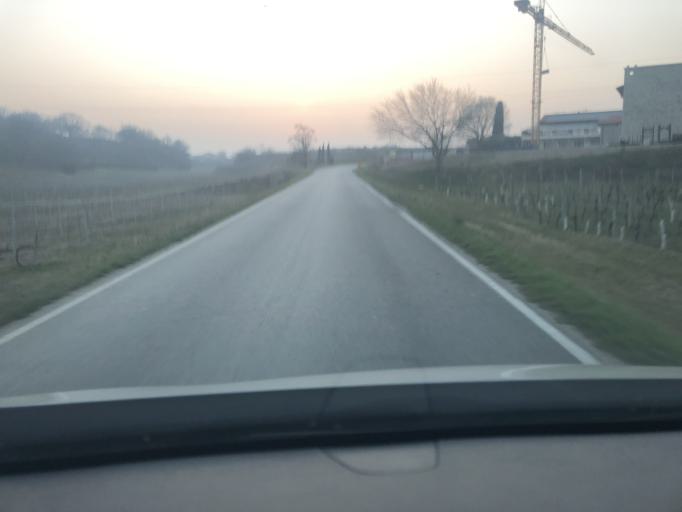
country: IT
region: Veneto
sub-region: Provincia di Verona
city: Sommacampagna
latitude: 45.3908
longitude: 10.8083
